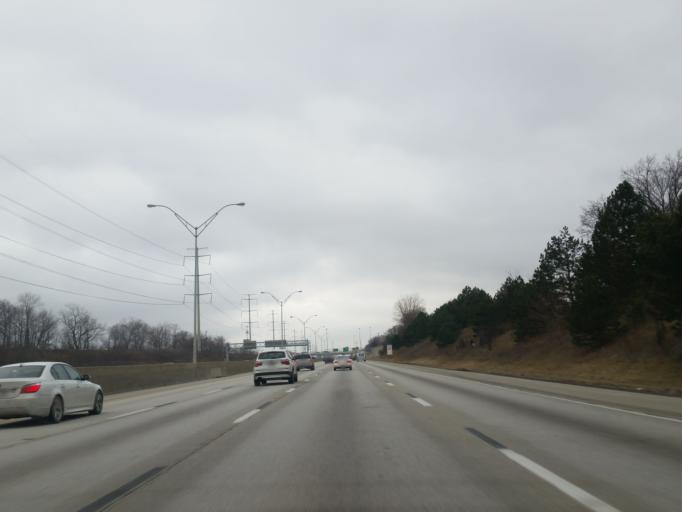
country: US
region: Ohio
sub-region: Cuyahoga County
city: Brooklyn Heights
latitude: 41.4212
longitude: -81.6985
